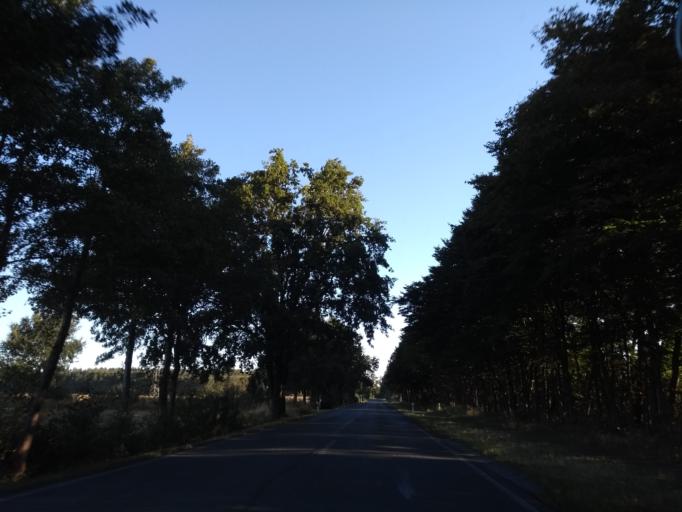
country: DE
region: Brandenburg
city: Lubbenau
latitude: 51.8455
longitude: 13.9490
